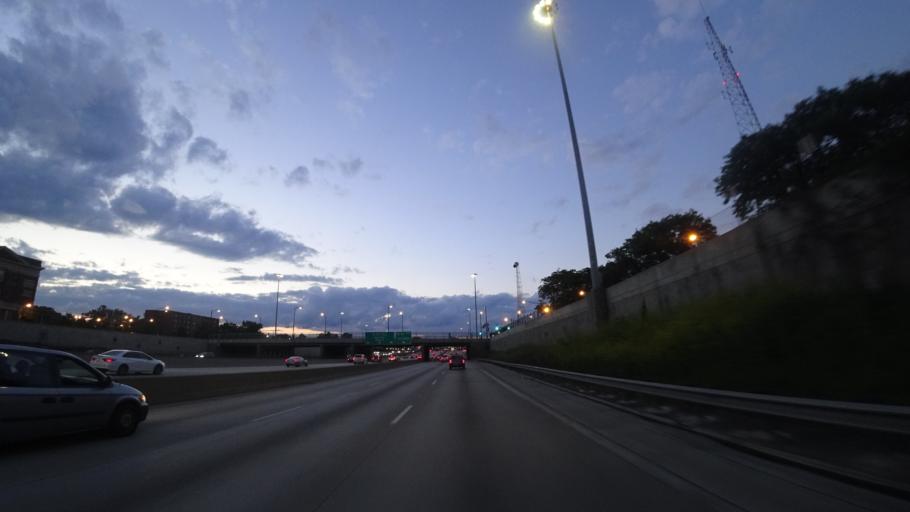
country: US
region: Illinois
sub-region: Cook County
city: Chicago
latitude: 41.8005
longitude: -87.6311
